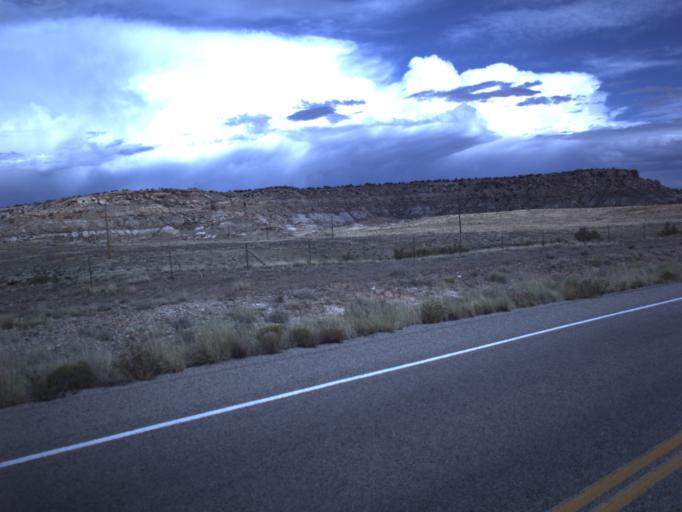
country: US
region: Colorado
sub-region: Montezuma County
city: Towaoc
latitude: 37.1650
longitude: -109.0738
